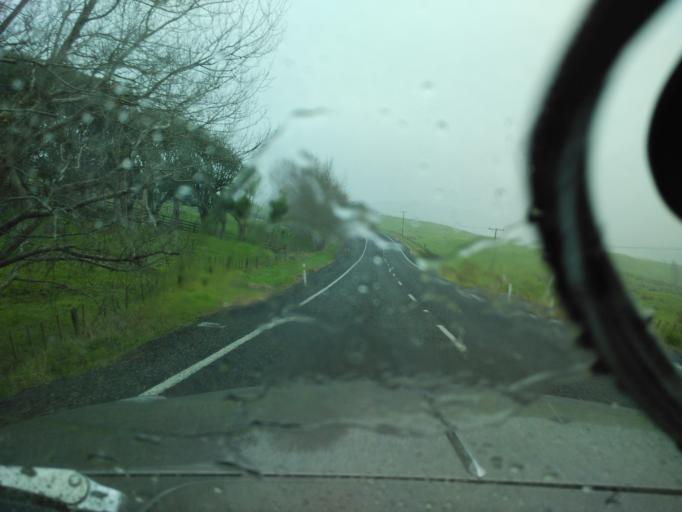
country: NZ
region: Auckland
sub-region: Auckland
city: Wellsford
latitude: -36.3986
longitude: 174.4459
